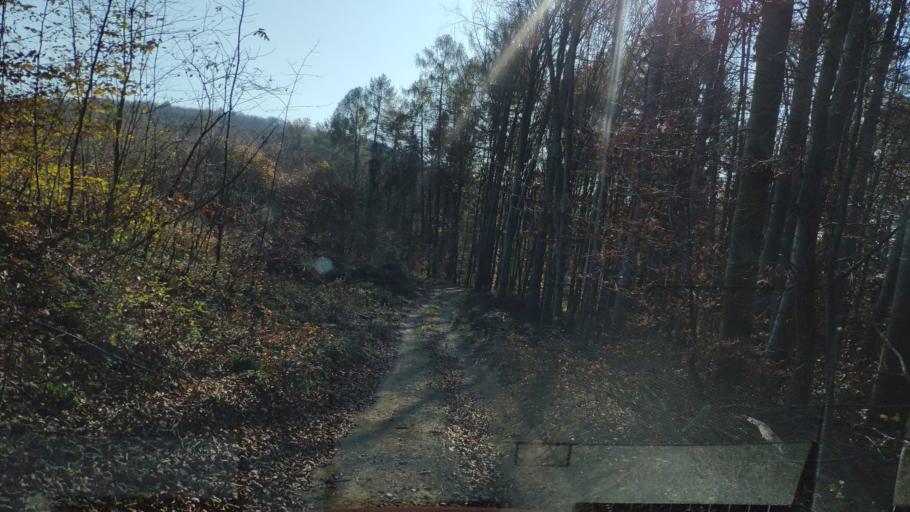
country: SK
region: Presovsky
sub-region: Okres Presov
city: Presov
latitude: 48.9004
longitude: 21.2194
